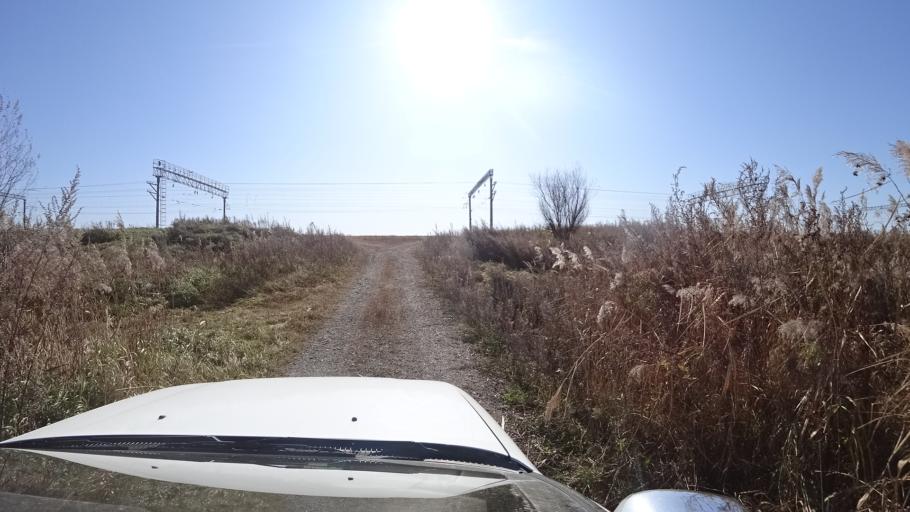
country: RU
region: Primorskiy
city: Dal'nerechensk
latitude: 45.9106
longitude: 133.7903
